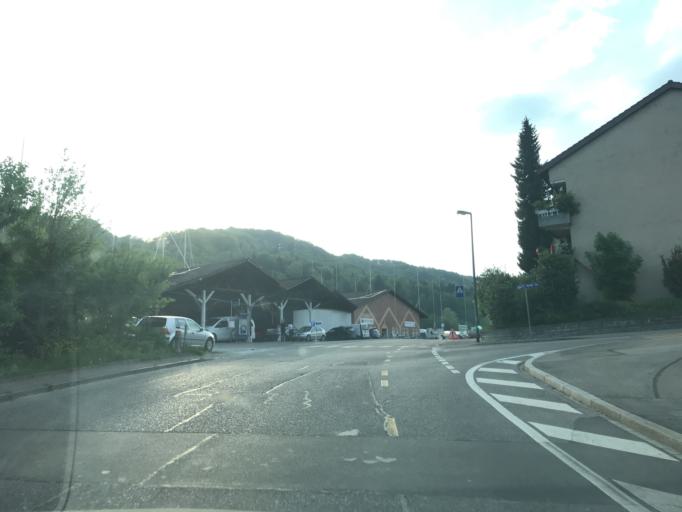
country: CH
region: Zurich
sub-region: Bezirk Winterthur
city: Toss
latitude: 47.4775
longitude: 8.7001
